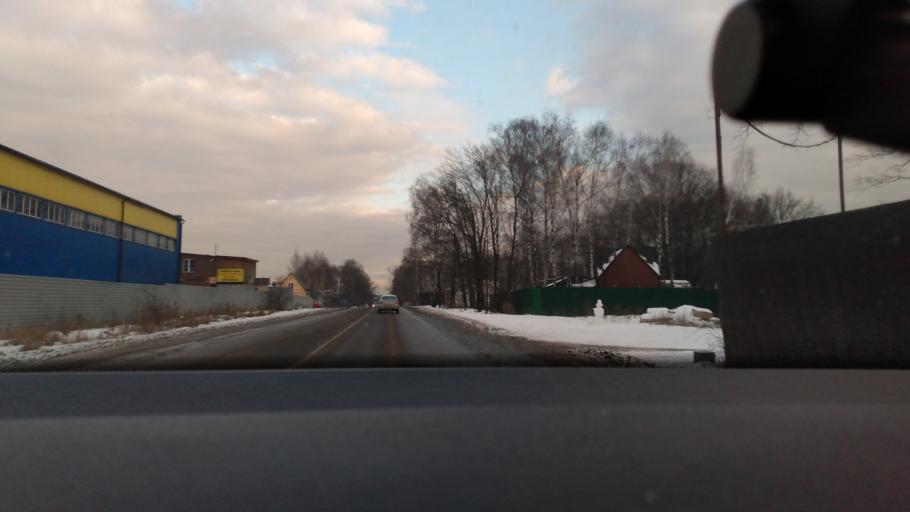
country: RU
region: Moskovskaya
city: Rodniki
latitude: 55.6956
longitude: 38.0586
